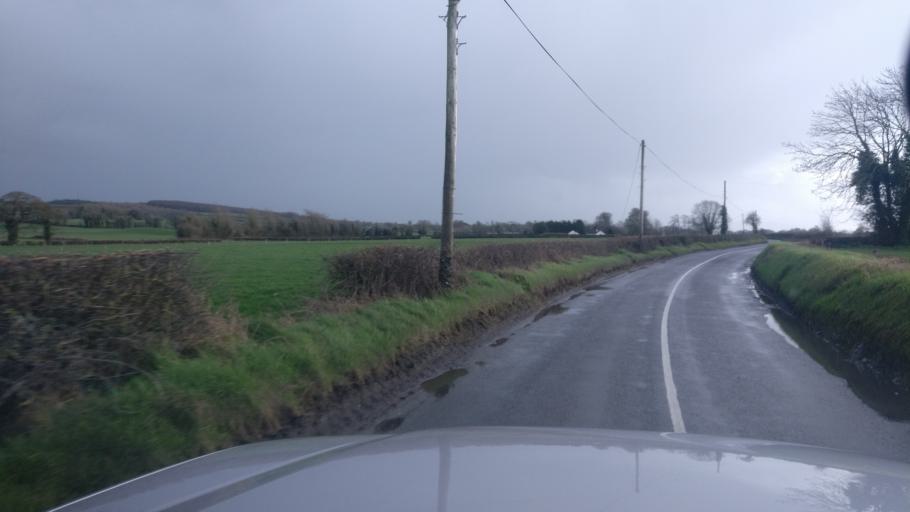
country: IE
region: Munster
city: Nenagh Bridge
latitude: 52.9601
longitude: -8.0805
